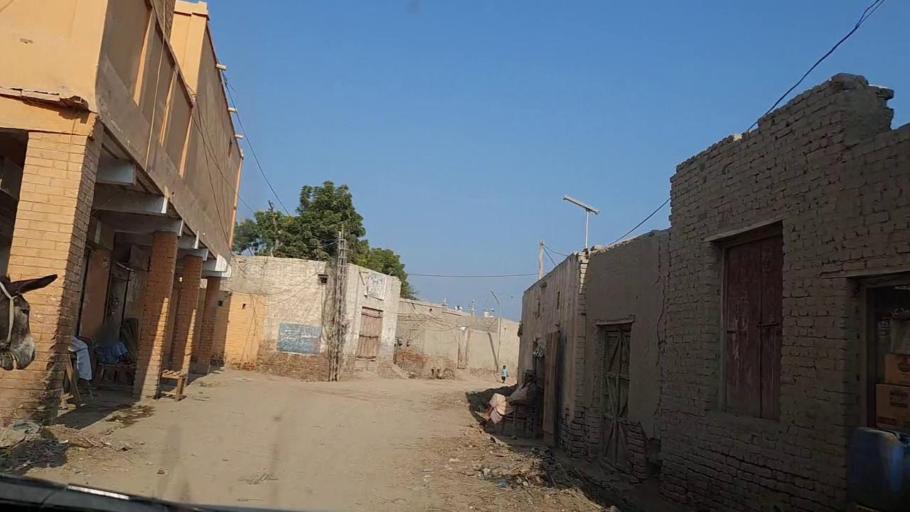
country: PK
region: Sindh
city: Moro
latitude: 26.7913
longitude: 67.9409
